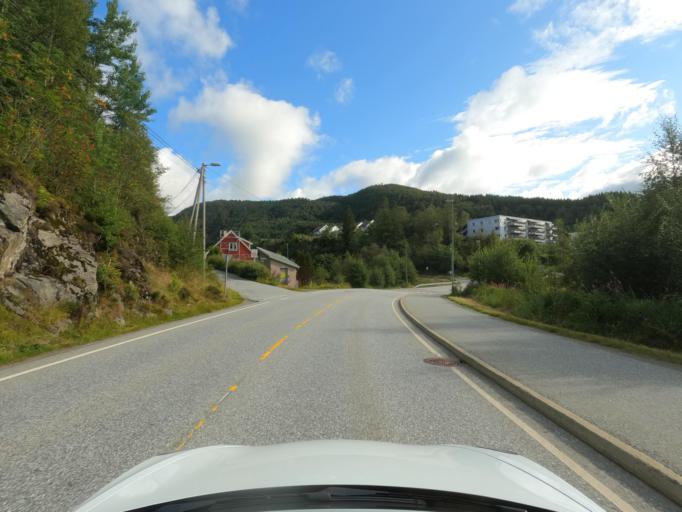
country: NO
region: Hordaland
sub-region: Bergen
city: Bergen
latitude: 60.3459
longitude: 5.3900
